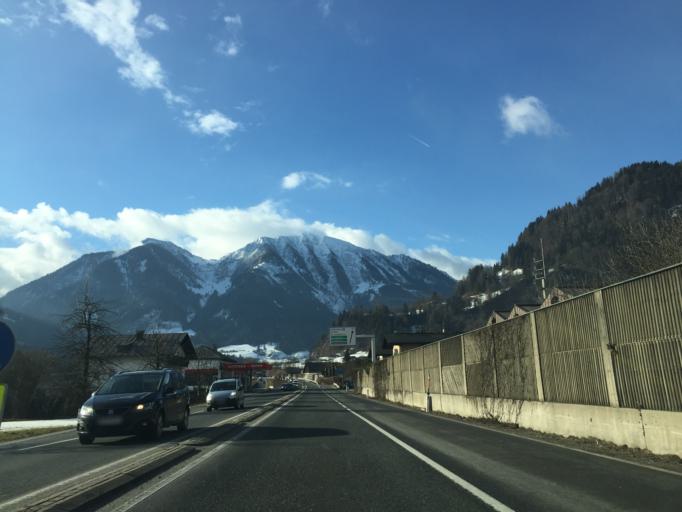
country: AT
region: Salzburg
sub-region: Politischer Bezirk Sankt Johann im Pongau
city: Sankt Johann im Pongau
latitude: 47.3421
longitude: 13.1912
